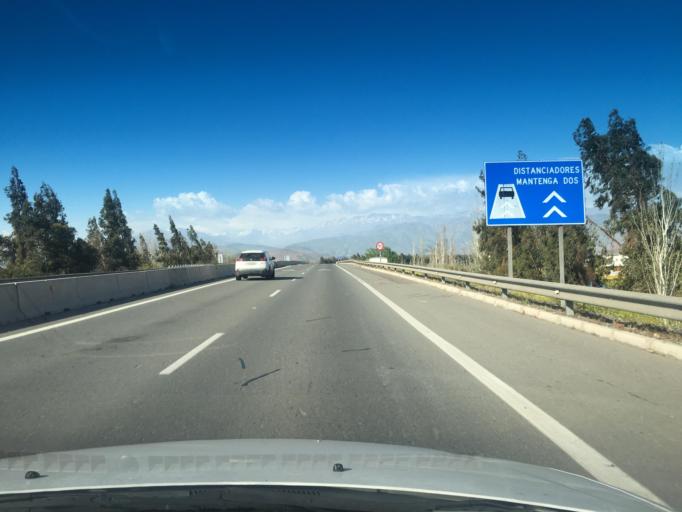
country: CL
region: Santiago Metropolitan
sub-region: Provincia de Chacabuco
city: Chicureo Abajo
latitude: -33.2978
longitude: -70.7252
